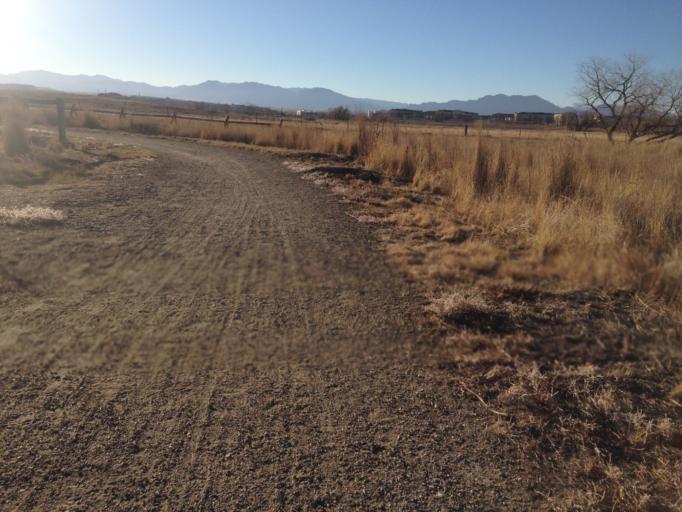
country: US
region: Colorado
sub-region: Broomfield County
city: Broomfield
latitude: 39.9415
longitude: -105.1088
